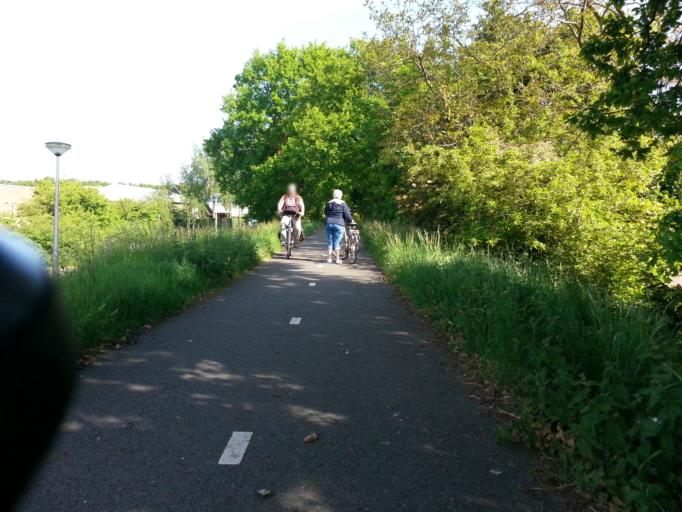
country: NL
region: Gelderland
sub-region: Berkelland
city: Eibergen
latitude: 52.1046
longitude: 6.6407
